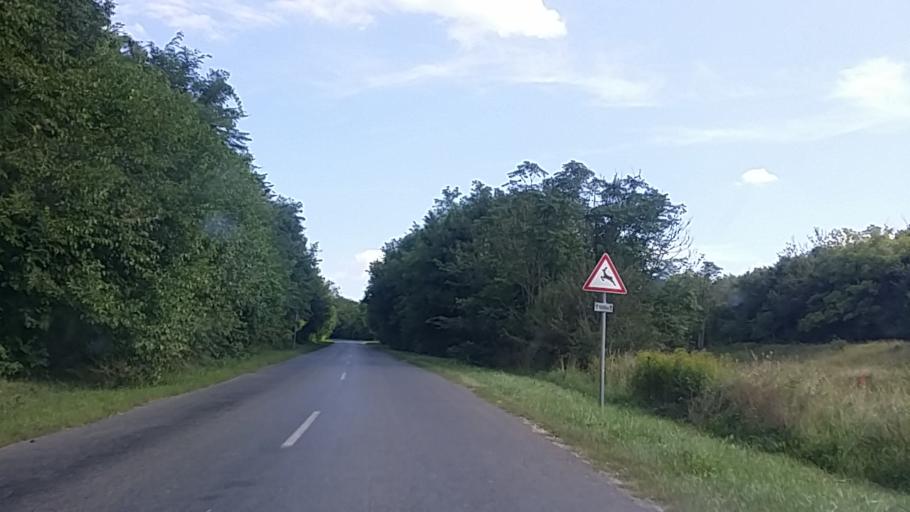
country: HU
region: Tolna
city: Gyonk
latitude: 46.5171
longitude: 18.5305
